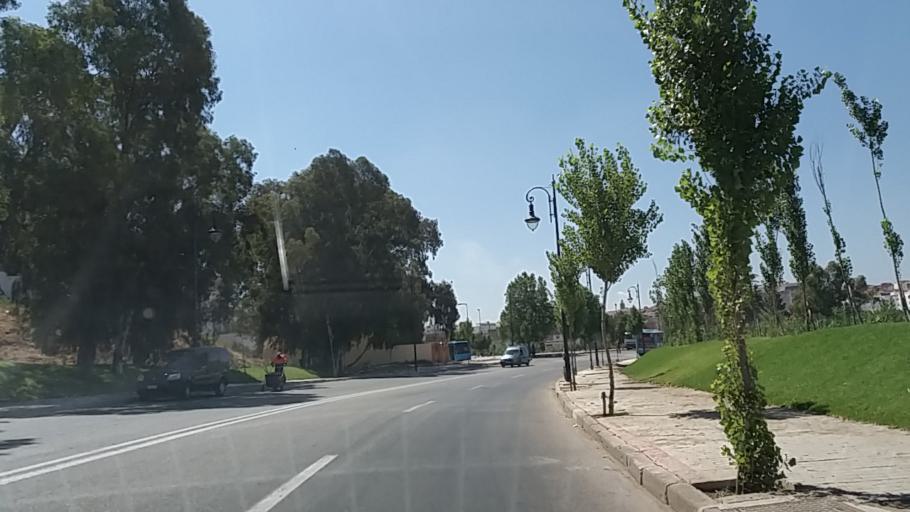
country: MA
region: Tanger-Tetouan
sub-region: Tanger-Assilah
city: Tangier
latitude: 35.7716
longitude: -5.7596
